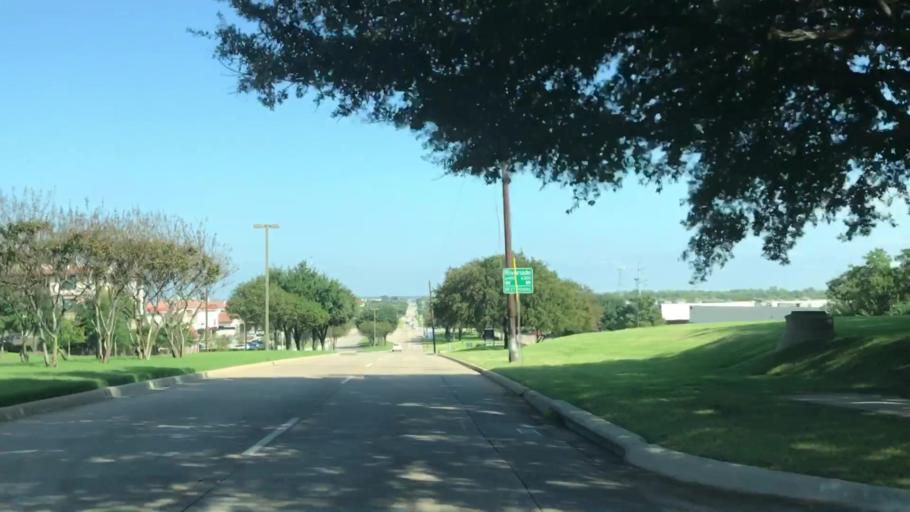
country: US
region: Texas
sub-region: Dallas County
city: Farmers Branch
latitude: 32.8957
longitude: -96.9424
